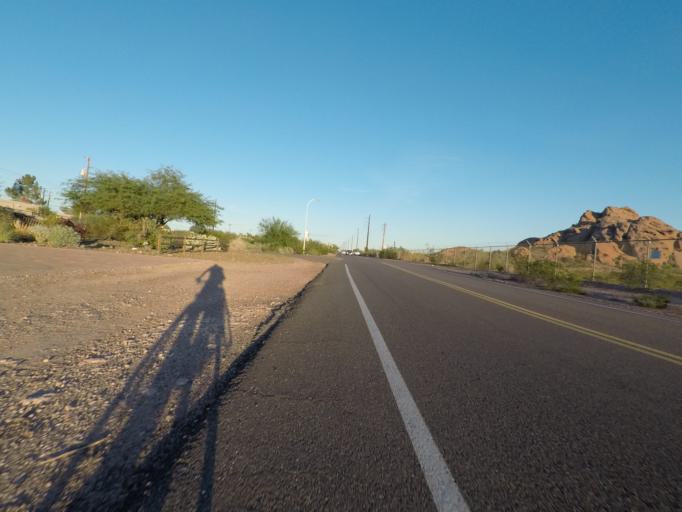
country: US
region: Arizona
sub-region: Maricopa County
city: Tempe Junction
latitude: 33.4728
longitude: -111.9629
